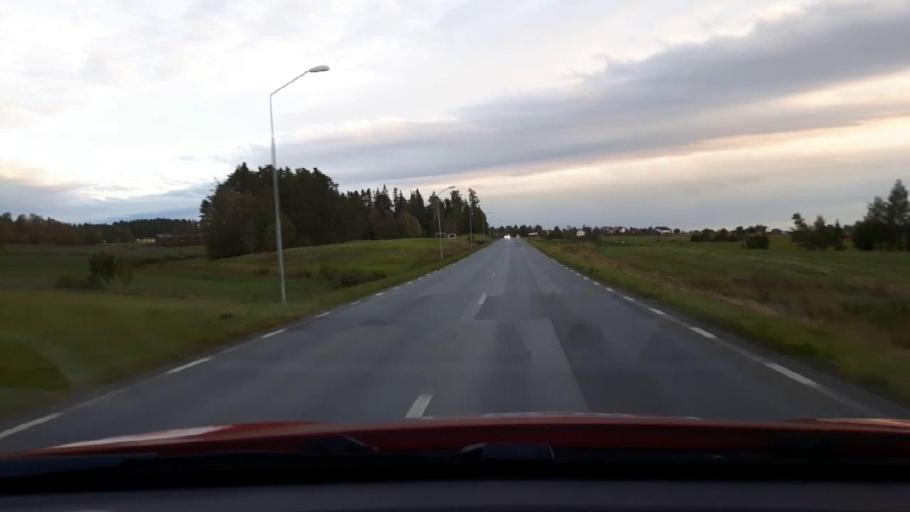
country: SE
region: Jaemtland
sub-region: Krokoms Kommun
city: Krokom
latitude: 63.1143
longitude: 14.4336
